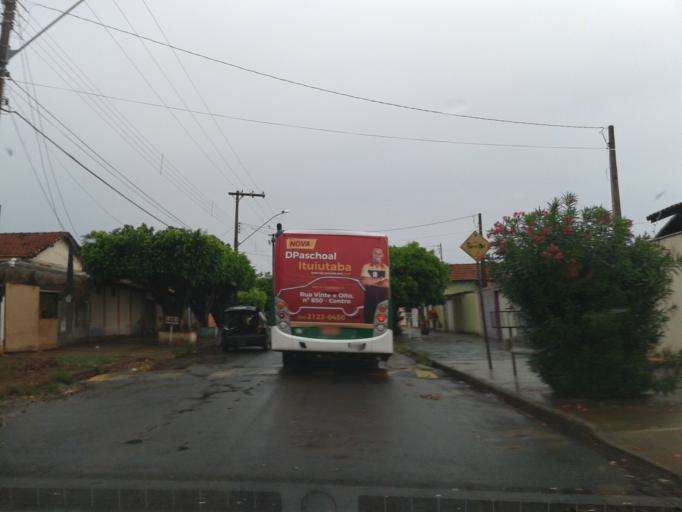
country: BR
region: Minas Gerais
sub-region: Ituiutaba
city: Ituiutaba
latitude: -18.9892
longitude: -49.4655
